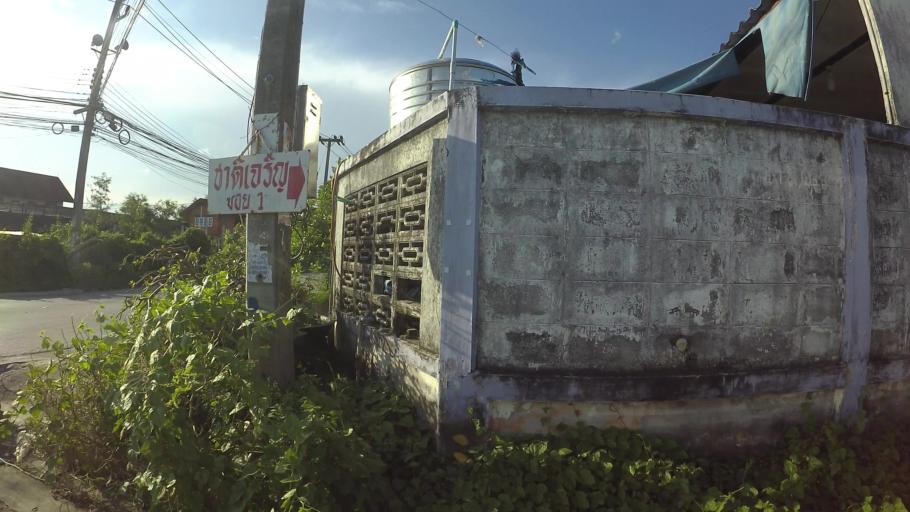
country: TH
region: Rayong
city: Rayong
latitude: 12.6896
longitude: 101.2804
